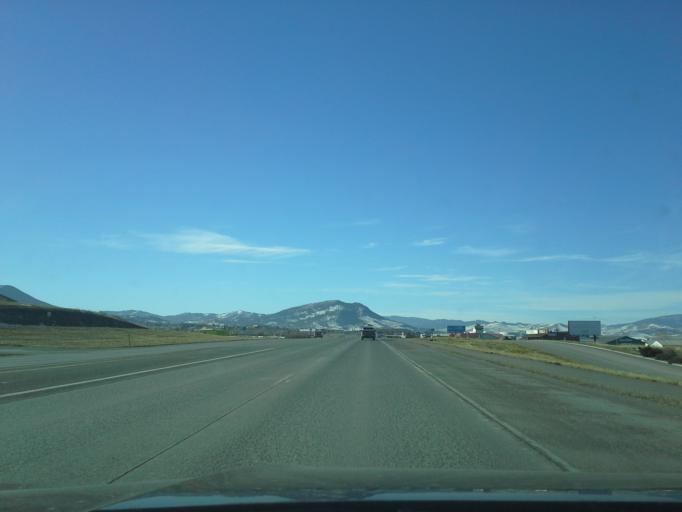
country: US
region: Montana
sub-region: Lewis and Clark County
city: Helena Valley Southeast
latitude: 46.5916
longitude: -111.9708
